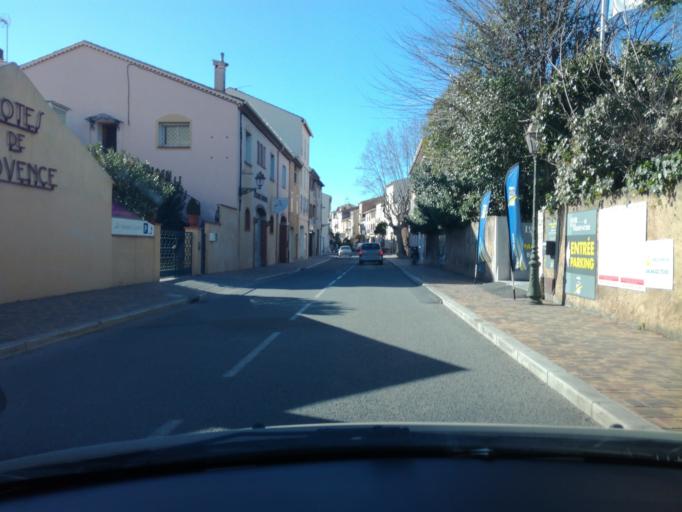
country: FR
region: Provence-Alpes-Cote d'Azur
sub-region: Departement du Var
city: Puget-sur-Argens
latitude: 43.4544
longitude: 6.6882
